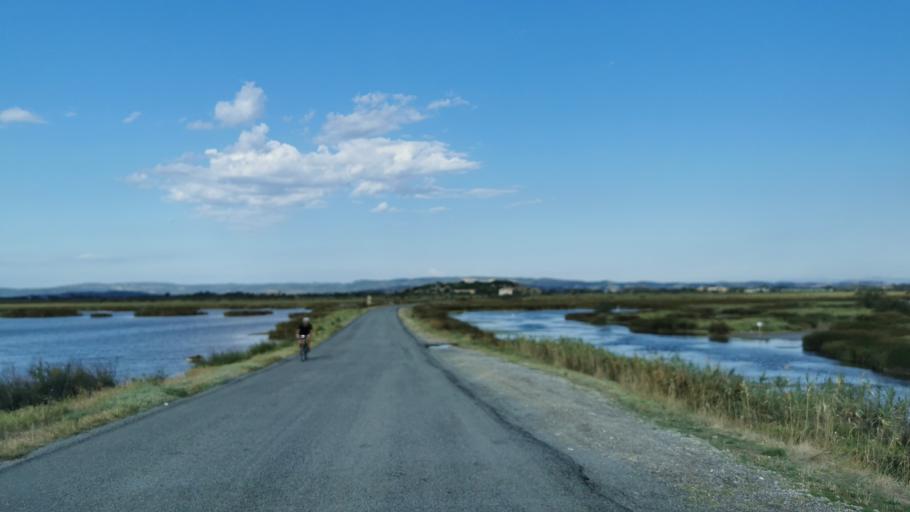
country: FR
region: Languedoc-Roussillon
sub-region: Departement de l'Aude
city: Gruissan
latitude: 43.1105
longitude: 3.0565
